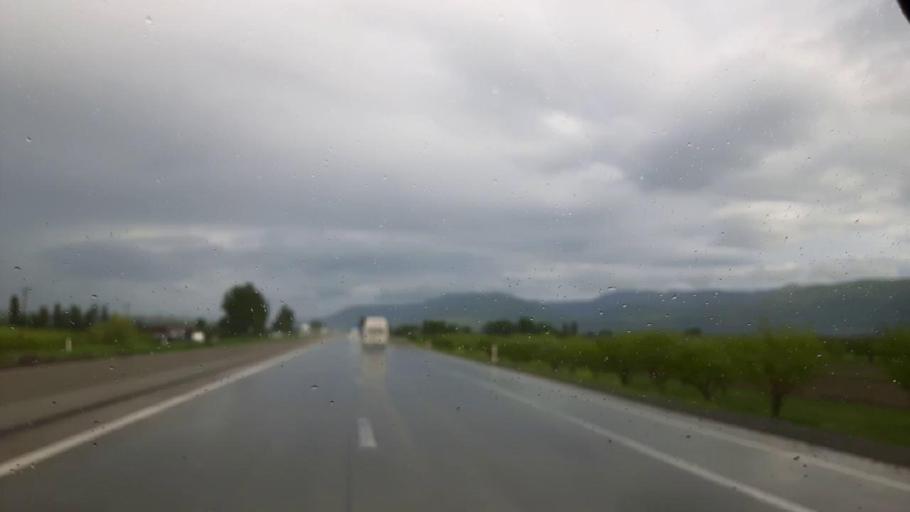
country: GE
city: Agara
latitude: 42.0364
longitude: 43.9386
